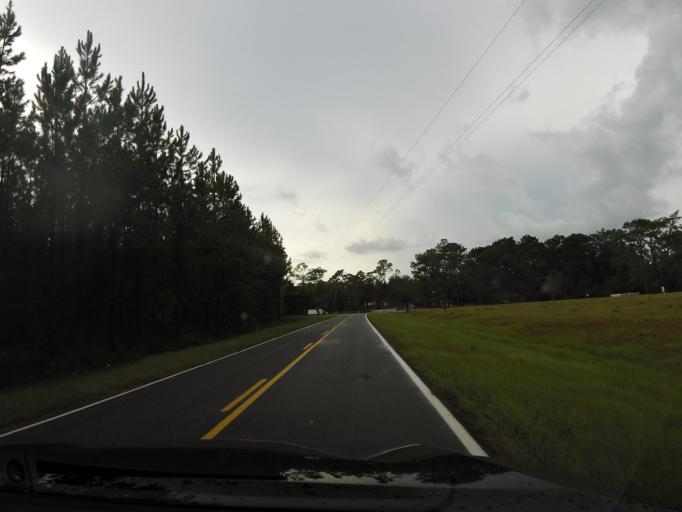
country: US
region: Georgia
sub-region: Wayne County
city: Jesup
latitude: 31.5541
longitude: -81.8946
